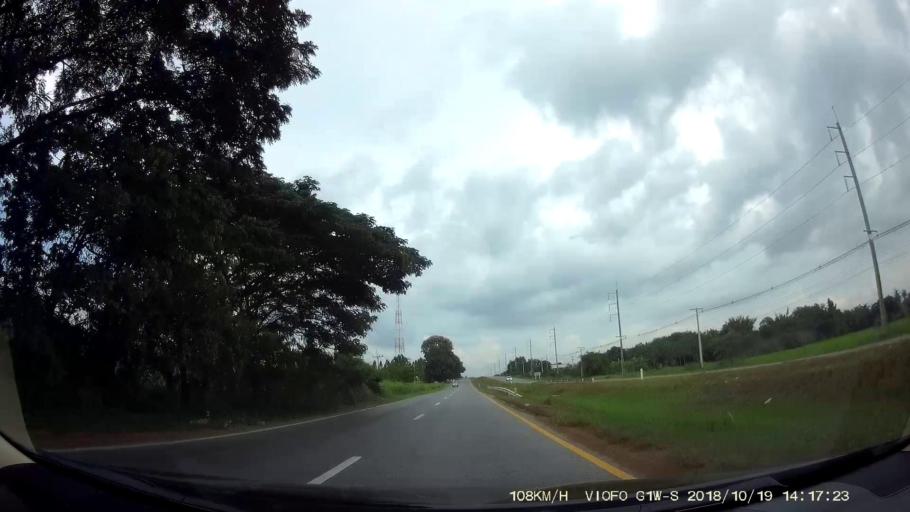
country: TH
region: Chaiyaphum
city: Khon Sawan
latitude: 16.0027
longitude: 102.2244
